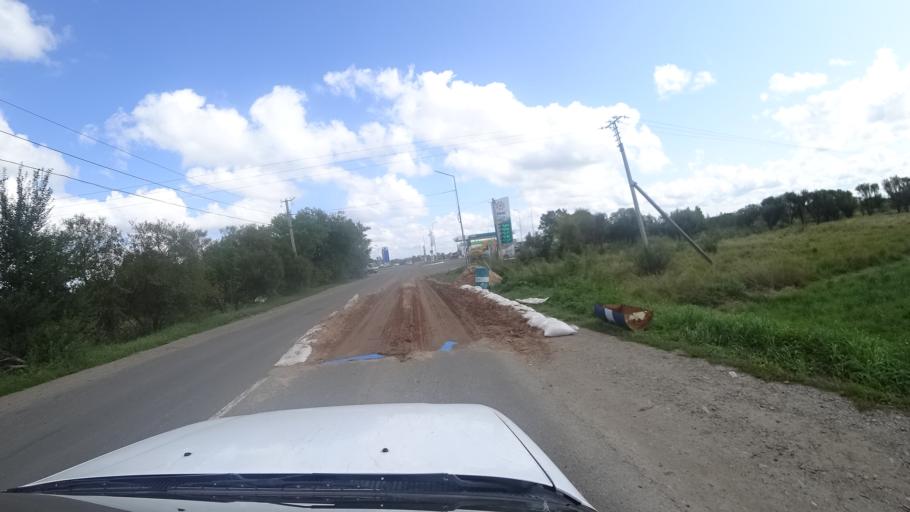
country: RU
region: Primorskiy
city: Dal'nerechensk
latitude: 45.9251
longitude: 133.7712
